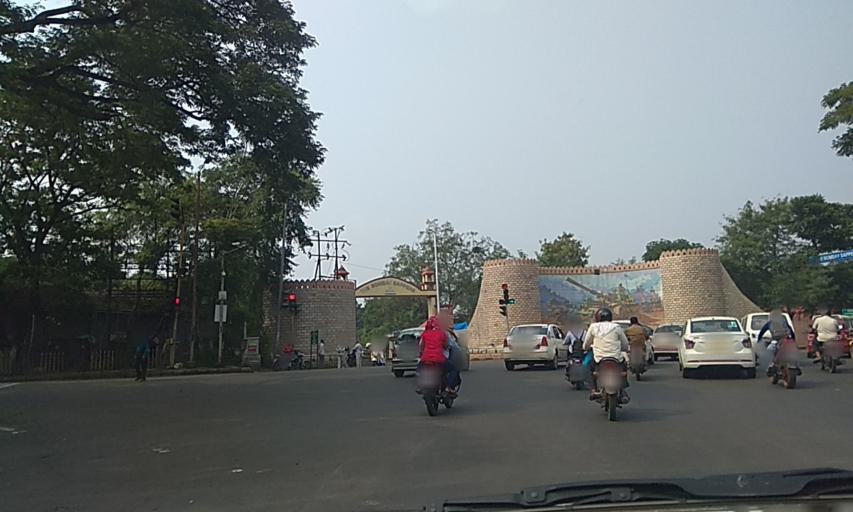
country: IN
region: Maharashtra
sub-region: Pune Division
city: Khadki
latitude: 18.5488
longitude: 73.8713
